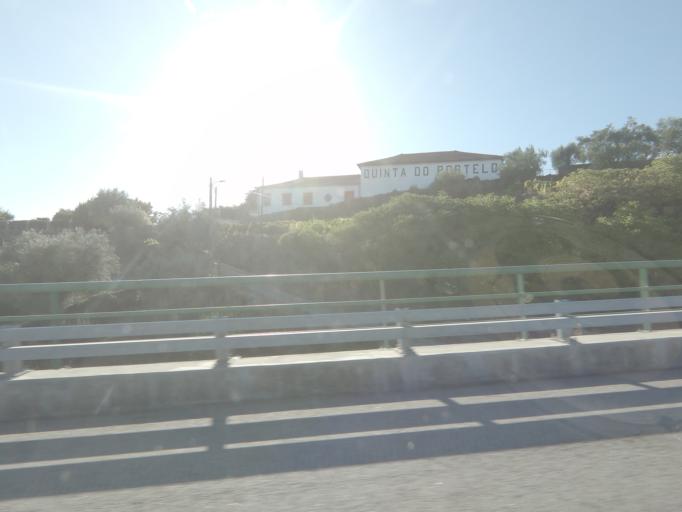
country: PT
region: Vila Real
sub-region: Peso da Regua
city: Peso da Regua
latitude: 41.1881
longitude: -7.7490
